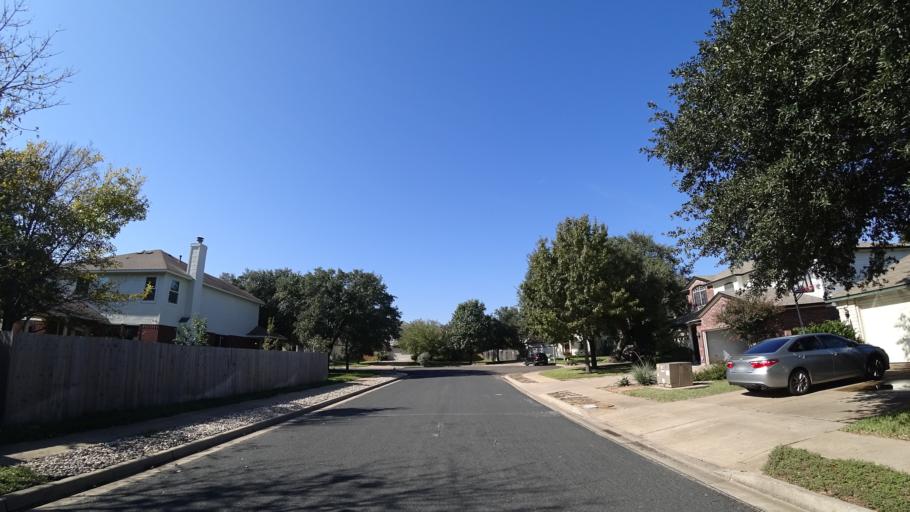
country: US
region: Texas
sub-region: Travis County
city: Shady Hollow
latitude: 30.2006
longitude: -97.8572
